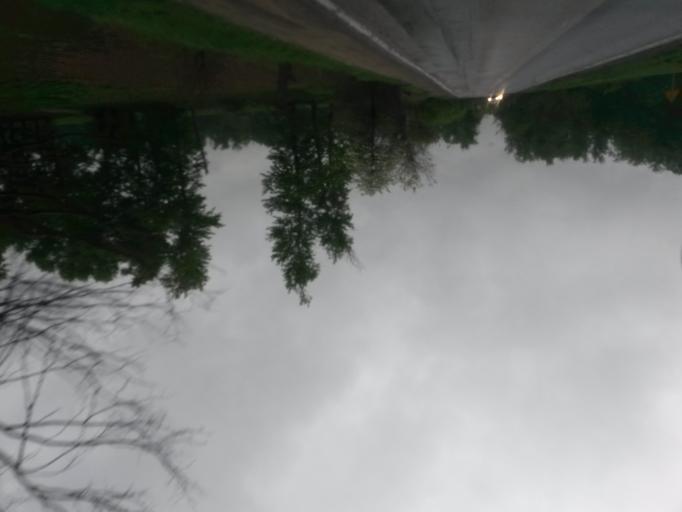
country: RU
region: Moskovskaya
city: Petrovskaya
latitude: 55.5585
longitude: 37.7801
